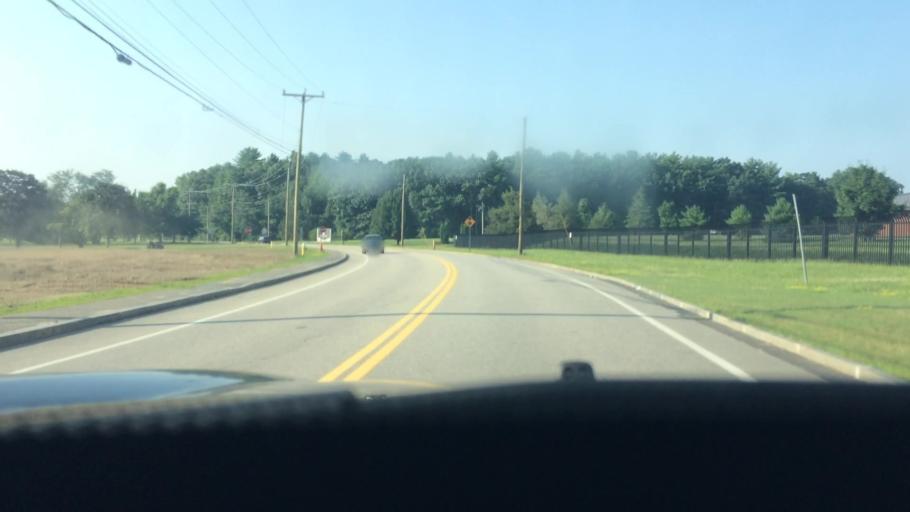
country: US
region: Maine
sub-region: York County
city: South Eliot
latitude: 43.0892
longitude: -70.8140
